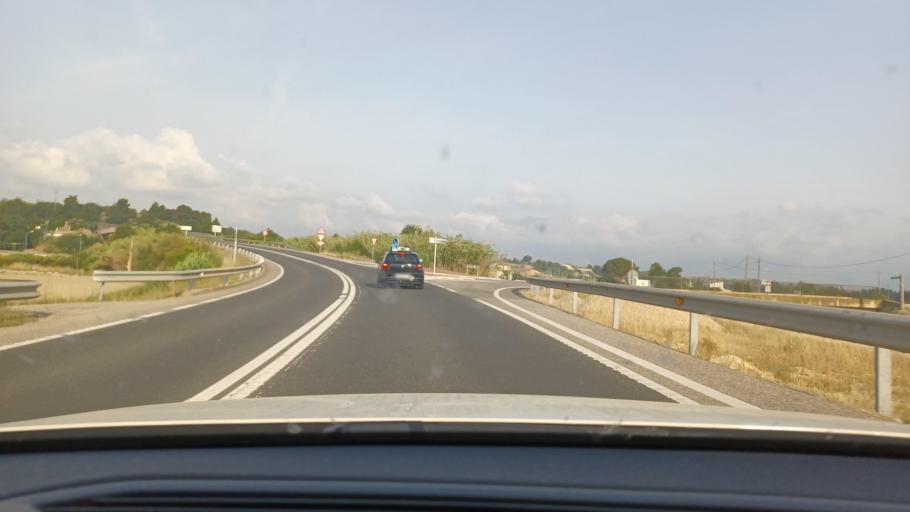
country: ES
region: Catalonia
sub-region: Provincia de Tarragona
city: Tortosa
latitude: 40.7763
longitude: 0.5150
